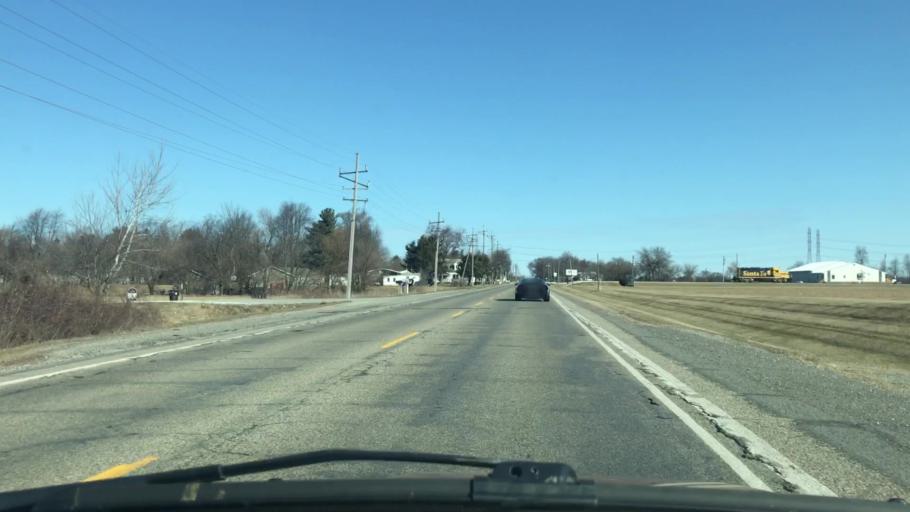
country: US
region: Indiana
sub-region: Porter County
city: Kouts
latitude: 41.3732
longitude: -87.0270
